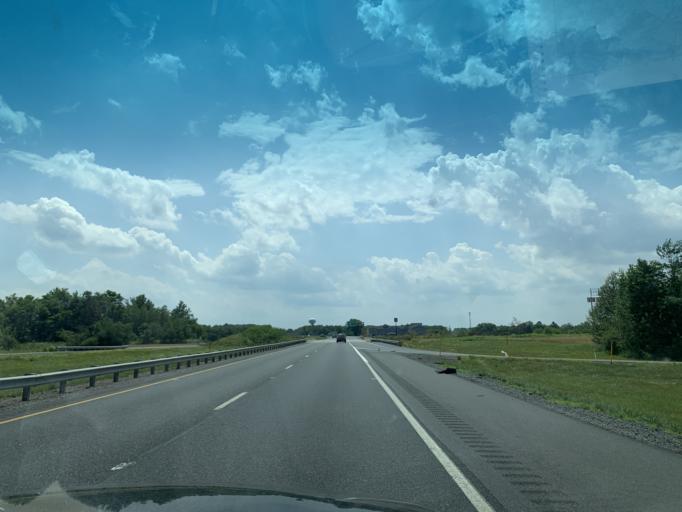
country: US
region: Pennsylvania
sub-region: Schuylkill County
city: Mahanoy City
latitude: 40.8114
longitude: -76.1035
